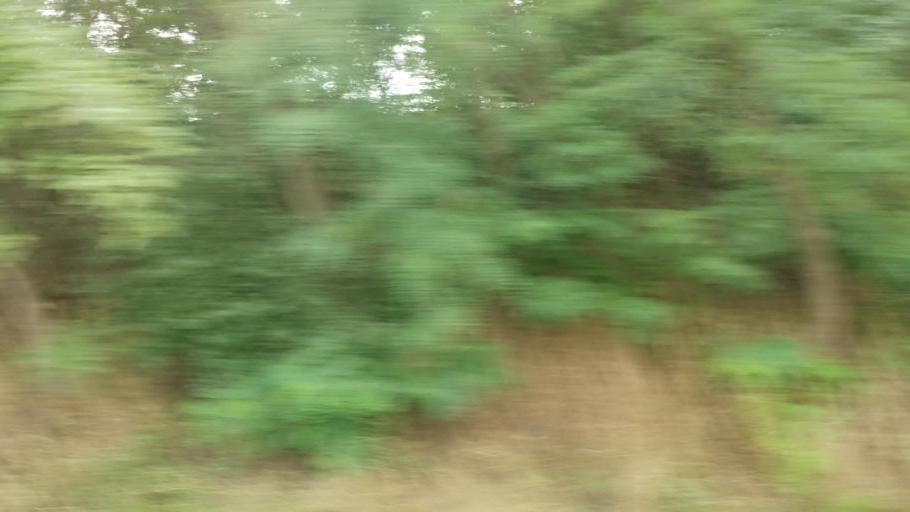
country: CZ
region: Central Bohemia
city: Horomerice
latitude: 50.1403
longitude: 14.3563
